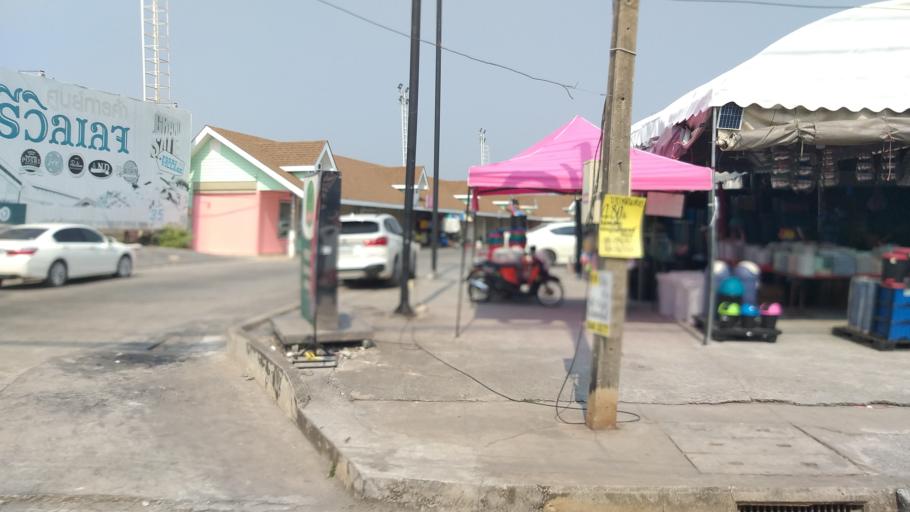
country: TH
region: Changwat Udon Thani
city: Udon Thani
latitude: 17.4147
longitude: 102.7752
